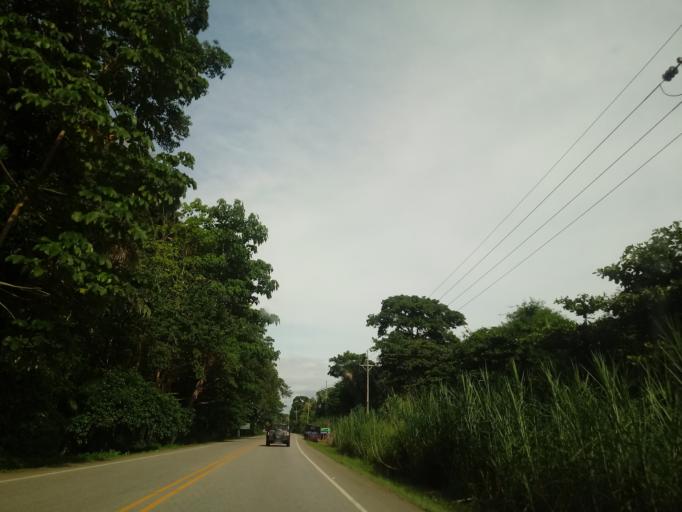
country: CR
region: San Jose
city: Daniel Flores
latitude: 9.1946
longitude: -83.7802
